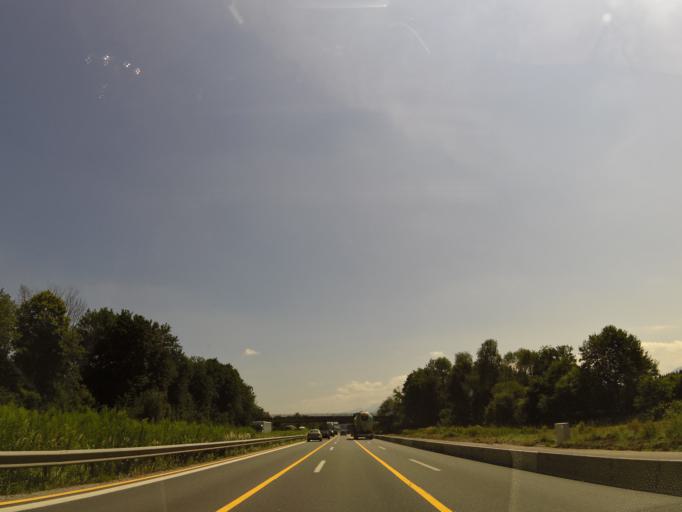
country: DE
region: Bavaria
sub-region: Upper Bavaria
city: Kolbermoor
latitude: 47.8133
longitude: 12.0735
